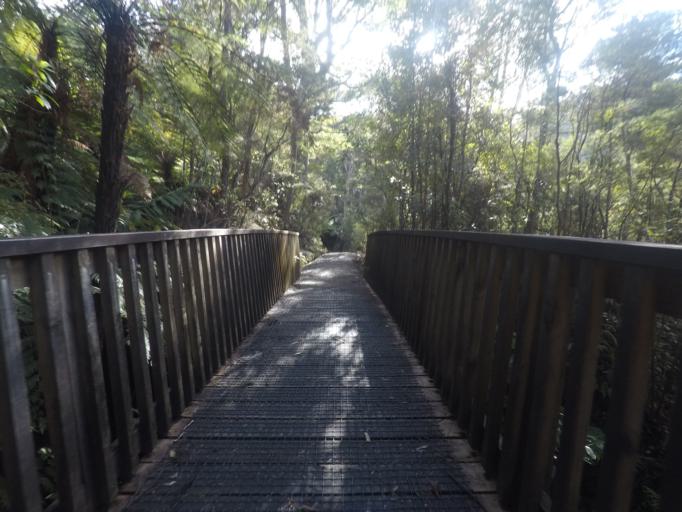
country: NZ
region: Auckland
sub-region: Auckland
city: Titirangi
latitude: -37.0031
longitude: 174.5578
